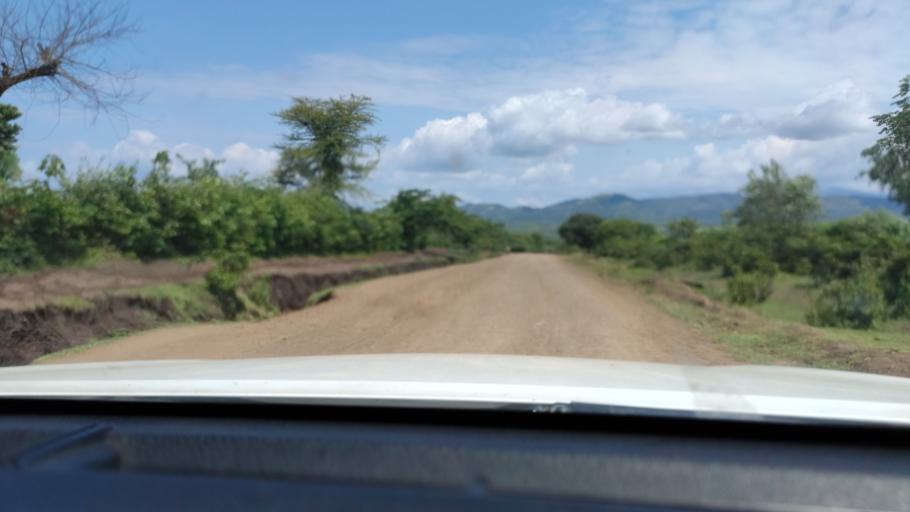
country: ET
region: Southern Nations, Nationalities, and People's Region
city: Felege Neway
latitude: 6.3653
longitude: 36.9867
